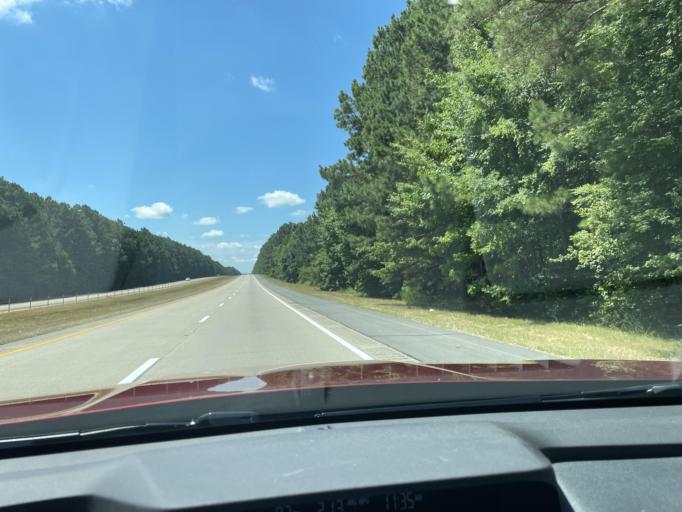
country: US
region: Arkansas
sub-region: Jefferson County
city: Redfield
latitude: 34.4580
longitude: -92.2032
